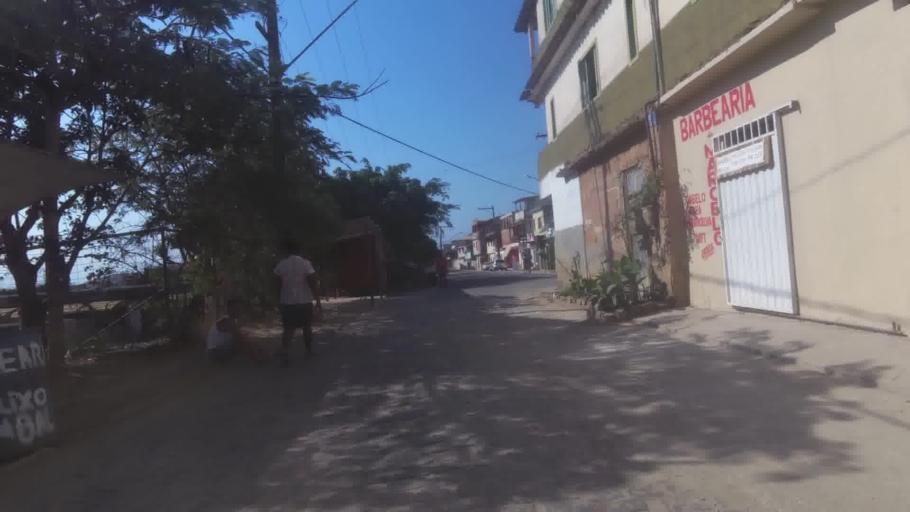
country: BR
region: Espirito Santo
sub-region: Itapemirim
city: Itapemirim
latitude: -21.0140
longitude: -40.8147
